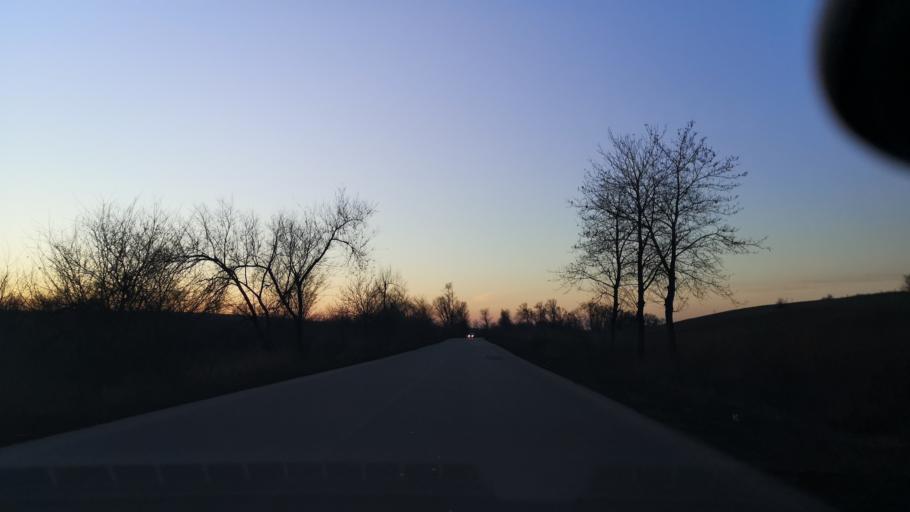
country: MD
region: Anenii Noi
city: Anenii Noi
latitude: 46.8887
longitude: 29.2527
